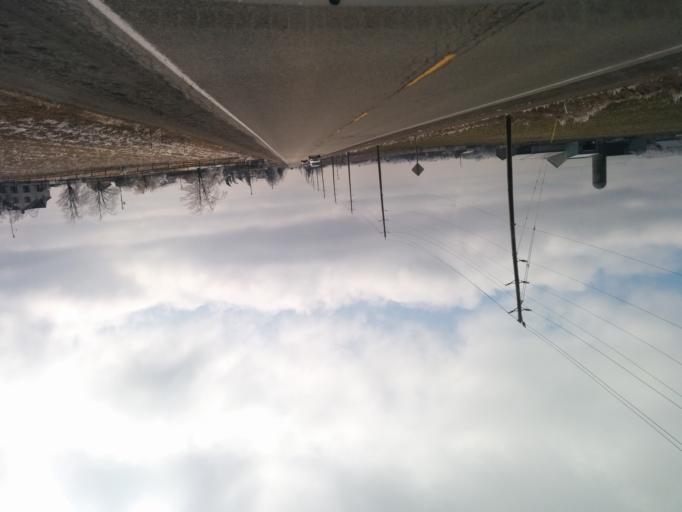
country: CA
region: Ontario
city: Waterloo
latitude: 43.6473
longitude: -80.5473
